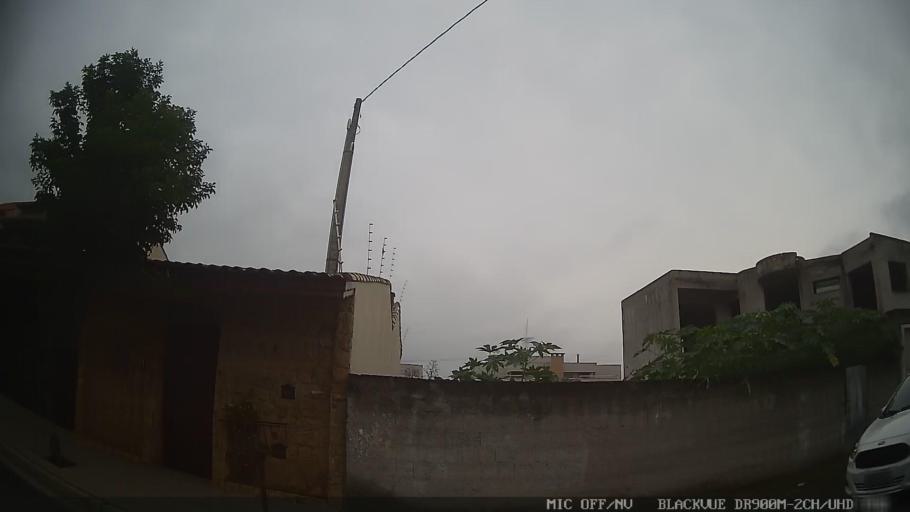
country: BR
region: Sao Paulo
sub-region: Mogi das Cruzes
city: Mogi das Cruzes
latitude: -23.5250
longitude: -46.1647
